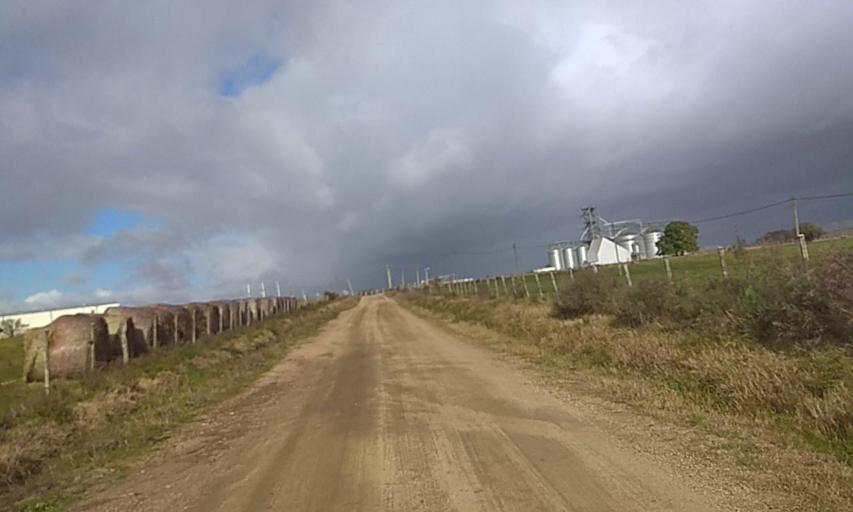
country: UY
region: Florida
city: Florida
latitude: -34.0896
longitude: -56.1873
